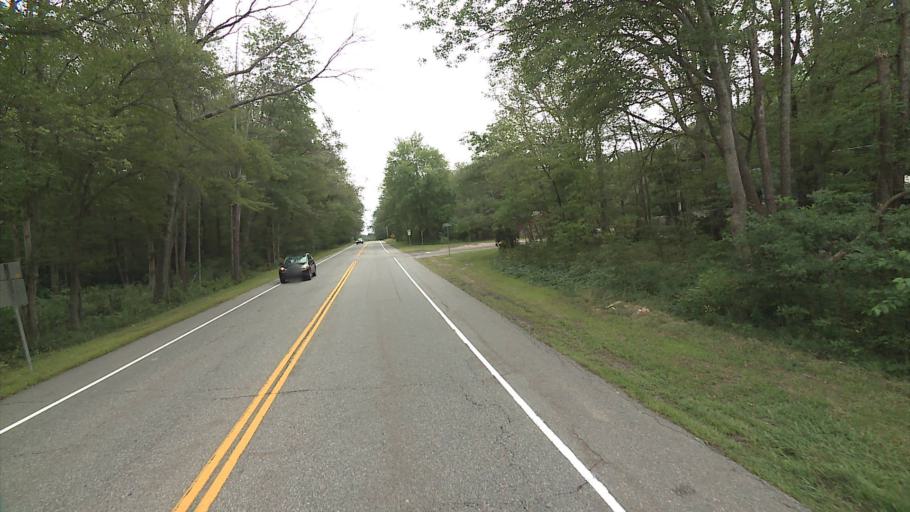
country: US
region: Connecticut
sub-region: Hartford County
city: Terramuggus
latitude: 41.6909
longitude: -72.4339
